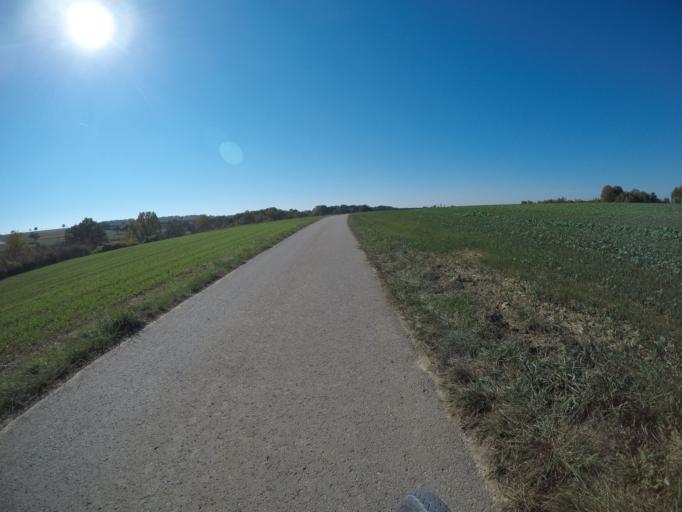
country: DE
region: Baden-Wuerttemberg
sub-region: Regierungsbezirk Stuttgart
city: Herrenberg
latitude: 48.5417
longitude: 8.8973
